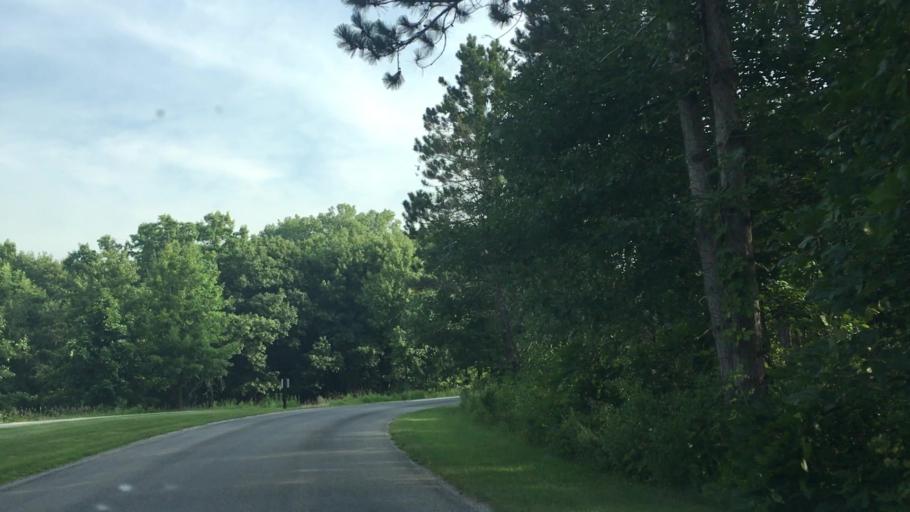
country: US
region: Iowa
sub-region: Johnson County
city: Tiffin
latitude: 41.7304
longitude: -91.7249
